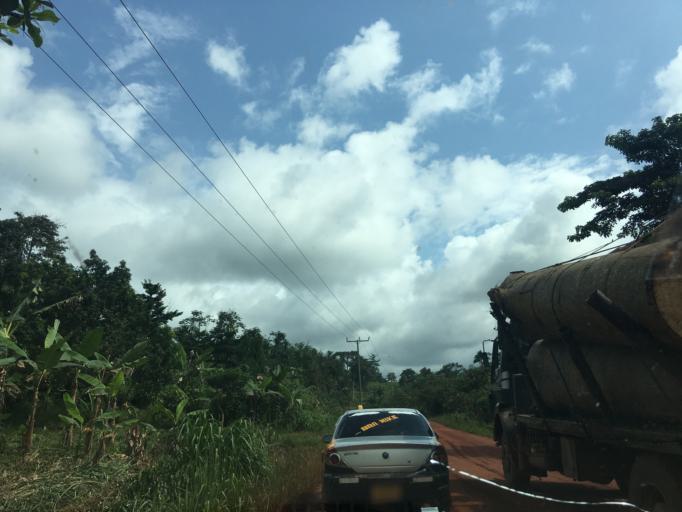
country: GH
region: Western
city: Wassa-Akropong
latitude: 5.7870
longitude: -2.3893
